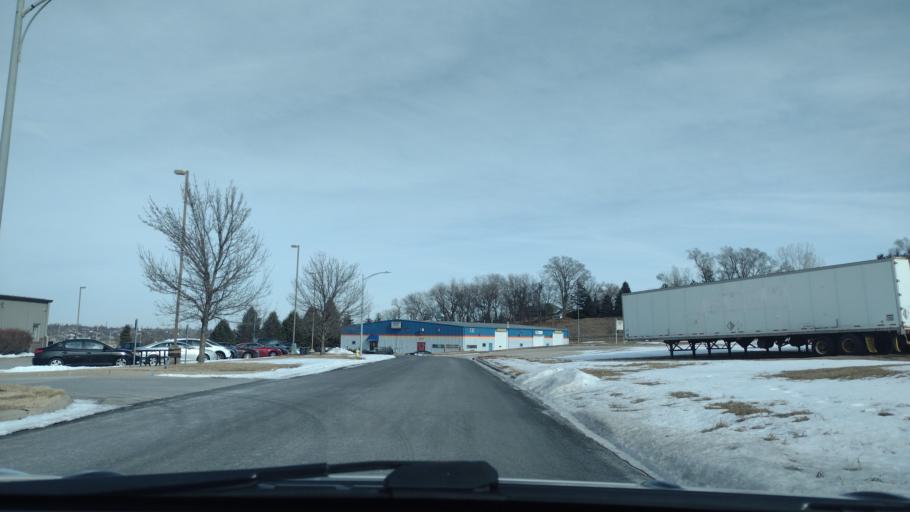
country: US
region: Nebraska
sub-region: Sarpy County
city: Papillion
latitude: 41.1418
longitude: -96.0254
